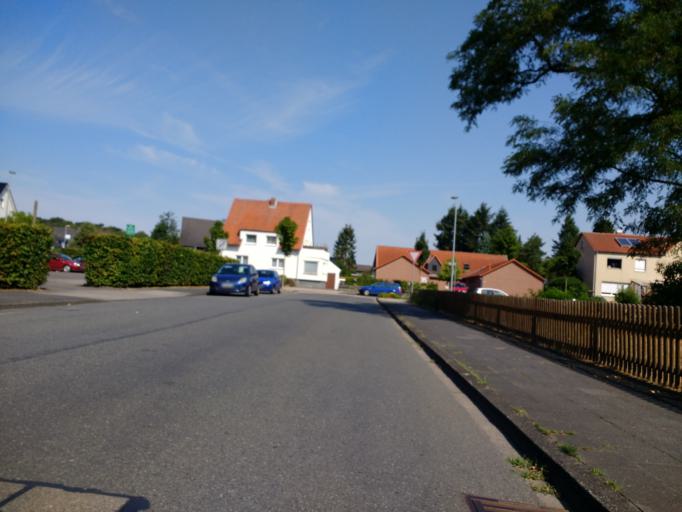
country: DE
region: Lower Saxony
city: Gifhorn
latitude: 52.4742
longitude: 10.5556
